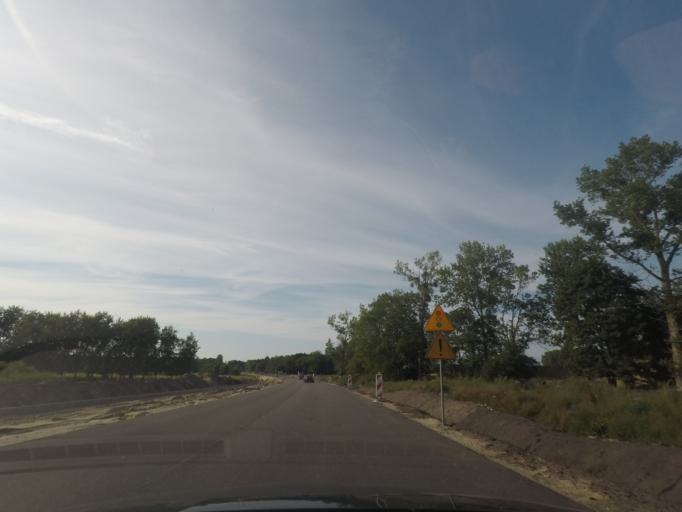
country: PL
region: Pomeranian Voivodeship
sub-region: Powiat leborski
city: Leba
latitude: 54.7273
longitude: 17.5687
